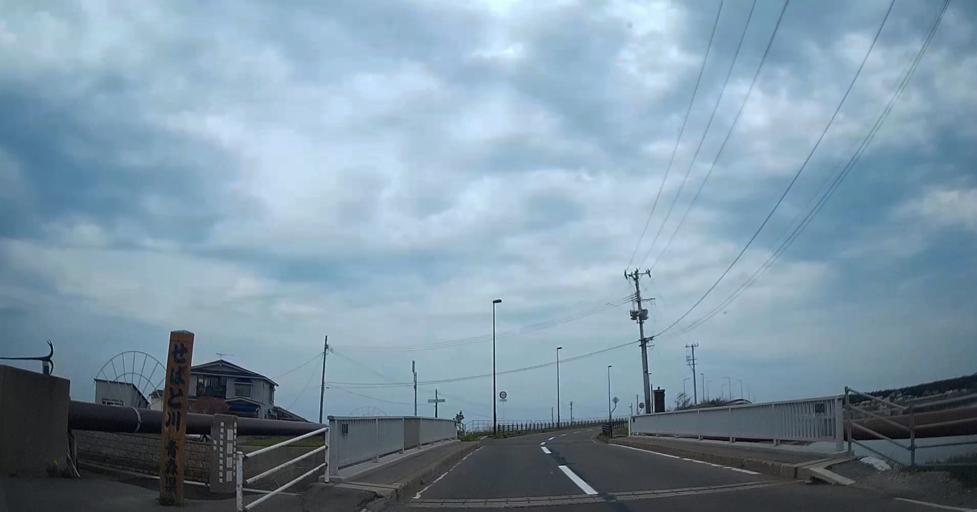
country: JP
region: Aomori
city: Shimokizukuri
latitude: 41.0368
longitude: 140.3287
